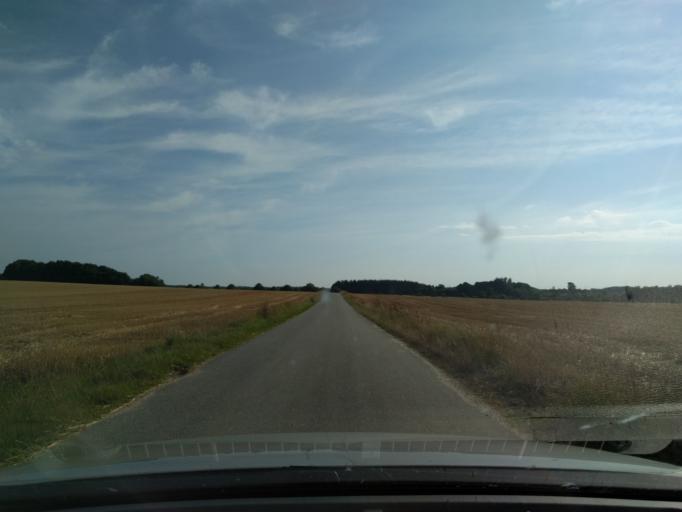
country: DK
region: Central Jutland
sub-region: Herning Kommune
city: Kibaek
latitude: 56.0567
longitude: 8.8826
